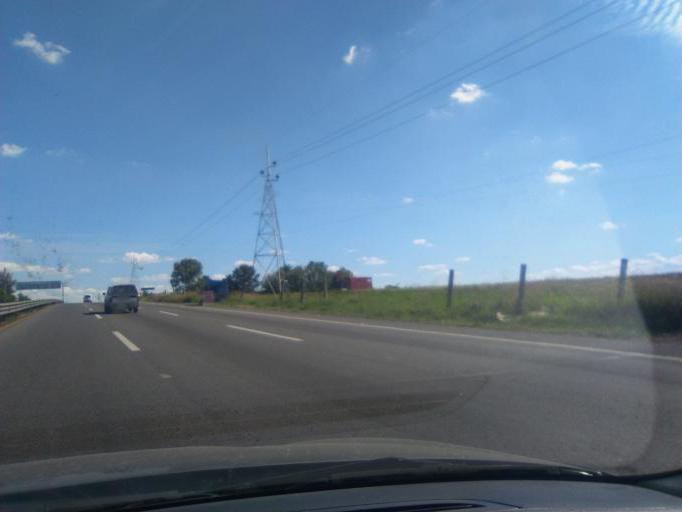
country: MX
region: Guanajuato
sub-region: Silao de la Victoria
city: San Antonio Texas
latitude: 20.9962
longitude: -101.5027
